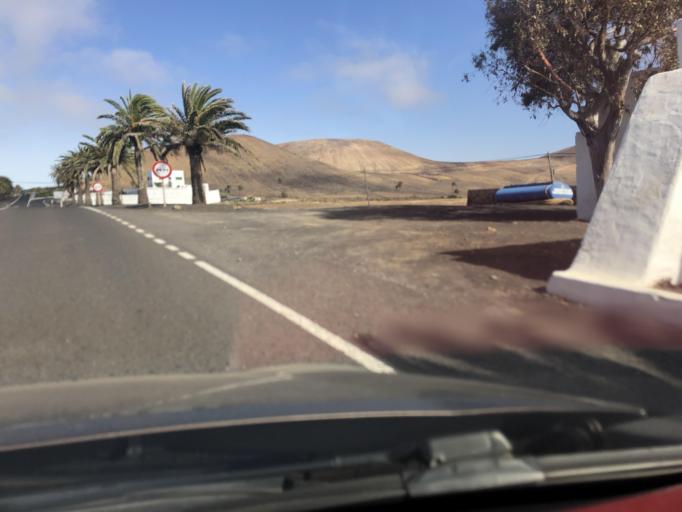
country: ES
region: Canary Islands
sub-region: Provincia de Las Palmas
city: Yaiza
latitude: 28.9523
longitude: -13.7614
